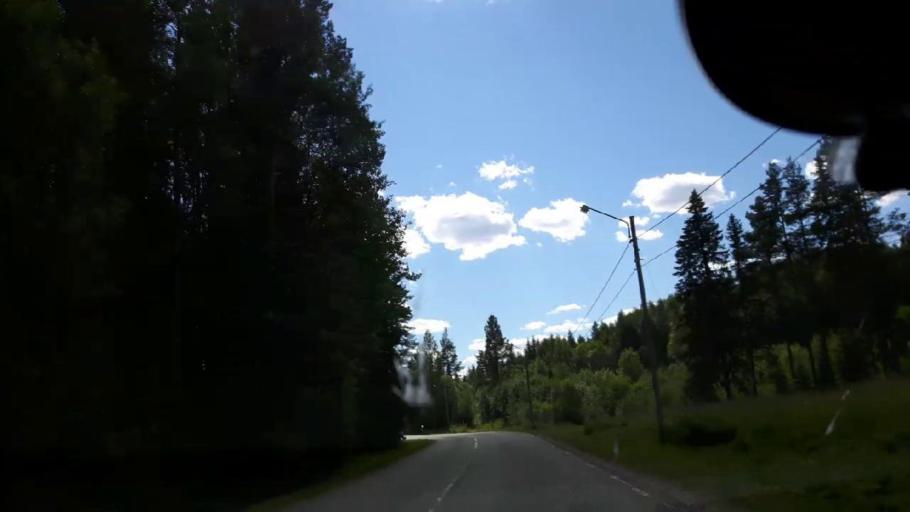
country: SE
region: Jaemtland
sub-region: Ragunda Kommun
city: Hammarstrand
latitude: 62.8955
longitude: 16.2252
